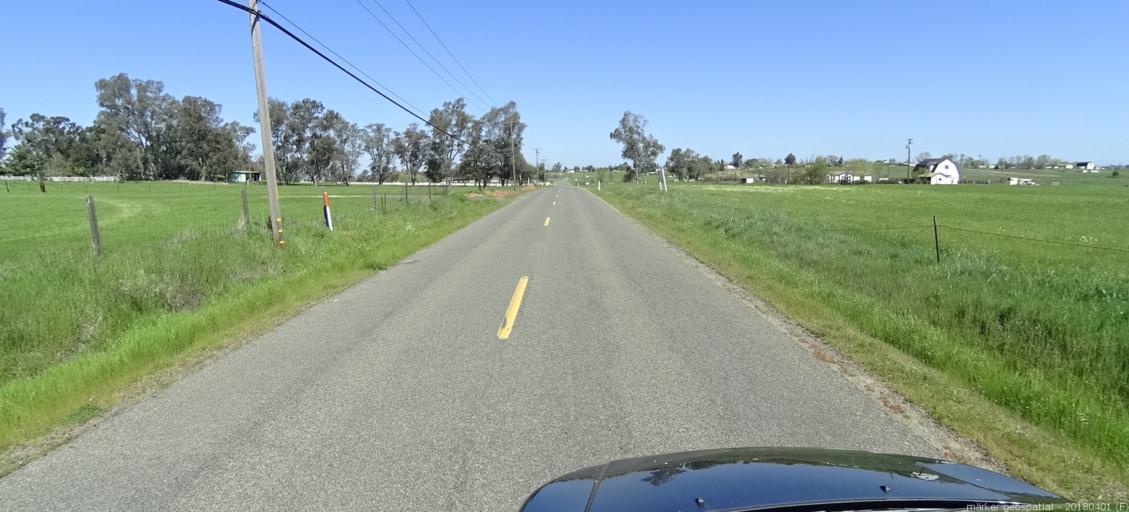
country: US
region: California
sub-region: Sacramento County
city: Wilton
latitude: 38.3927
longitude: -121.2422
